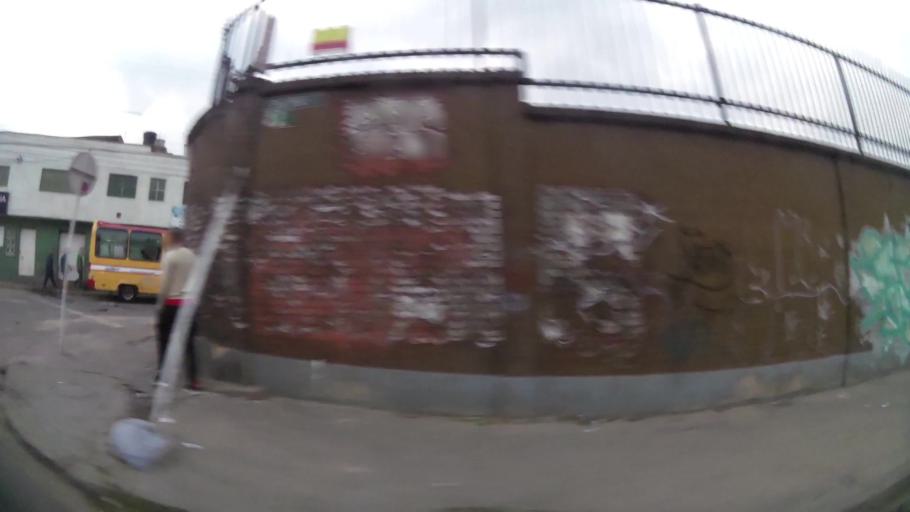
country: CO
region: Bogota D.C.
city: Bogota
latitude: 4.5863
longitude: -74.1231
